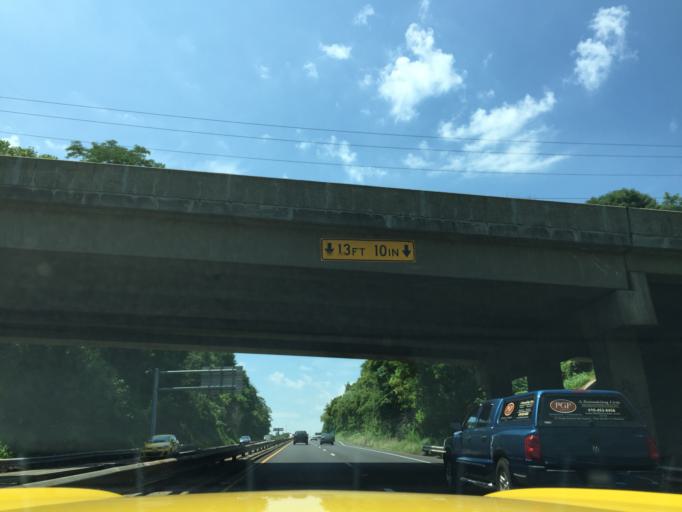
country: US
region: Pennsylvania
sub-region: Bucks County
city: Trevose
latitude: 40.1439
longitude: -74.9557
